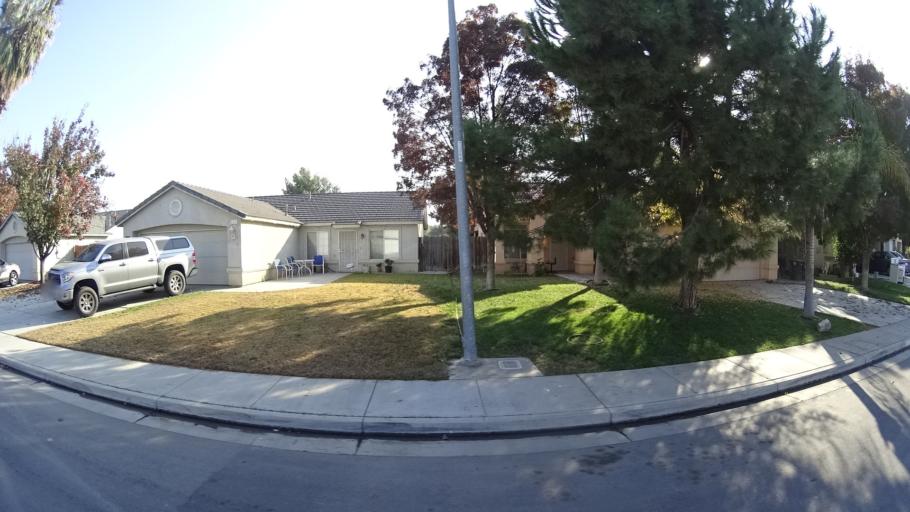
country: US
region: California
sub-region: Kern County
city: Greenfield
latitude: 35.2877
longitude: -119.0154
